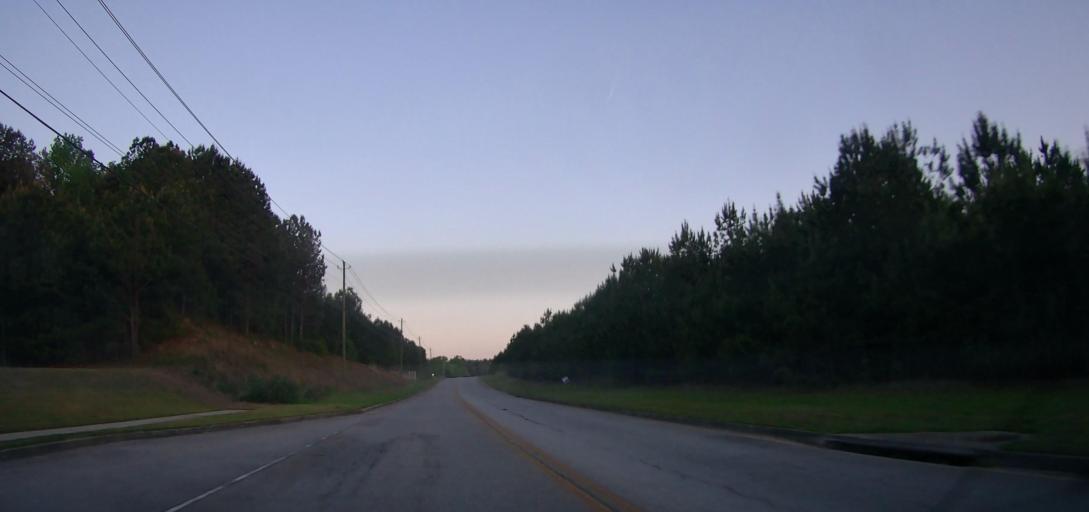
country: US
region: Georgia
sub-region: Henry County
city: Stockbridge
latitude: 33.4976
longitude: -84.2202
